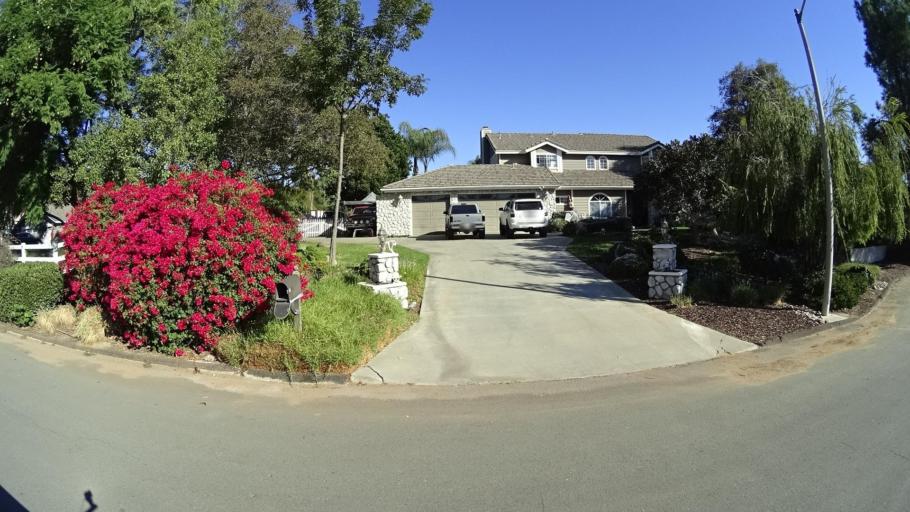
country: US
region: California
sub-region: San Diego County
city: Jamul
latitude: 32.7096
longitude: -116.8745
